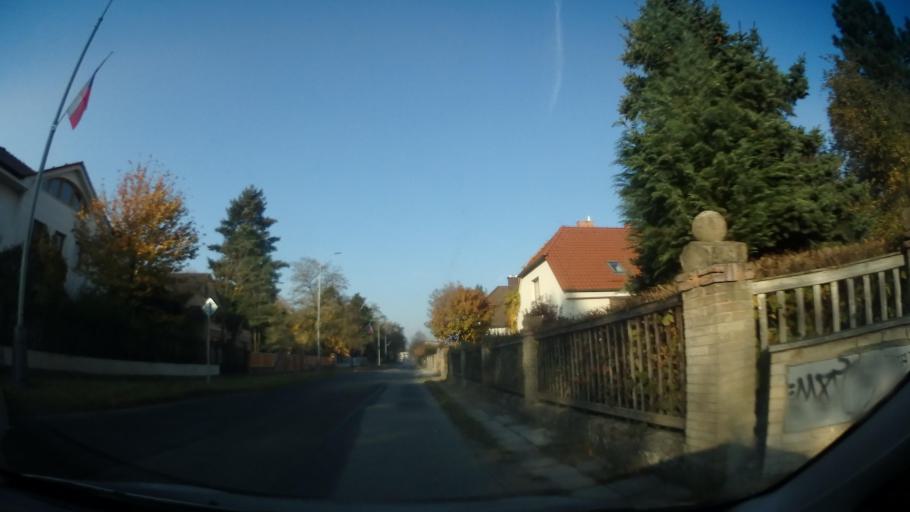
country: CZ
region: Central Bohemia
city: Sestajovice
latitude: 50.0991
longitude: 14.6770
